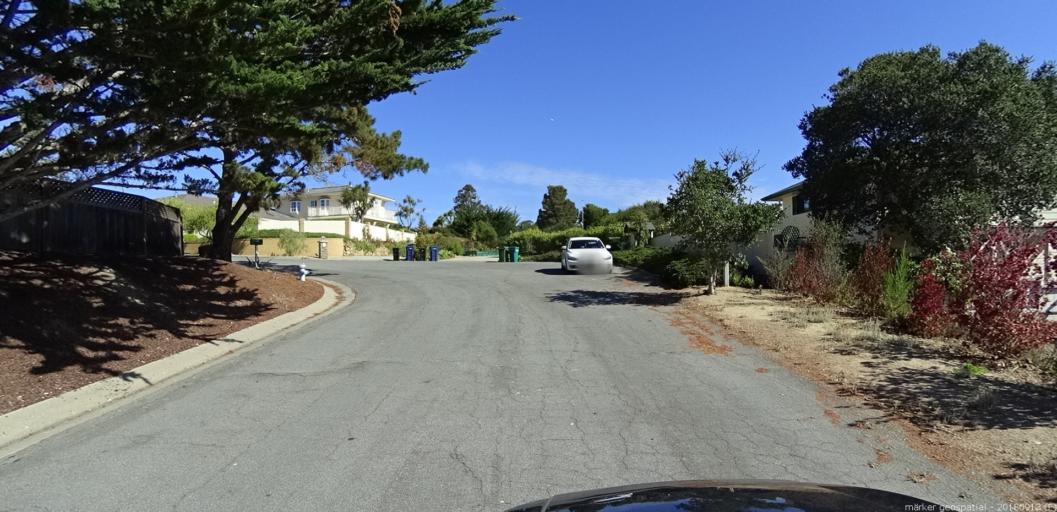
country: US
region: California
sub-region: Monterey County
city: Carmel-by-the-Sea
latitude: 36.5507
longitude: -121.9037
